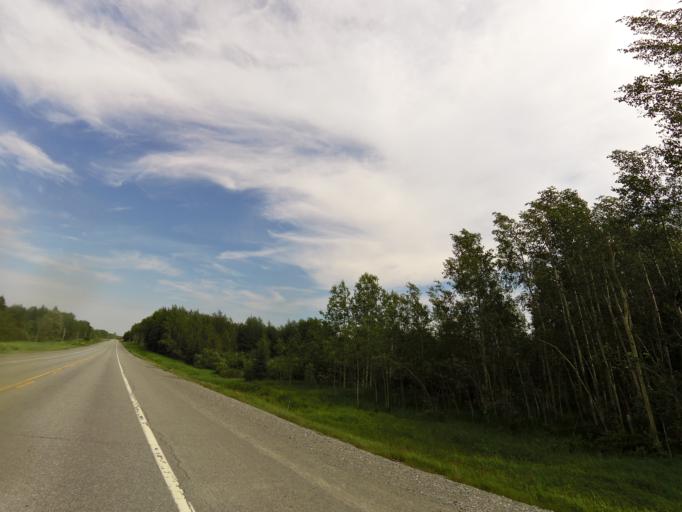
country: CA
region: Quebec
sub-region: Abitibi-Temiscamingue
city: Malartic
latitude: 48.2334
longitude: -78.4252
